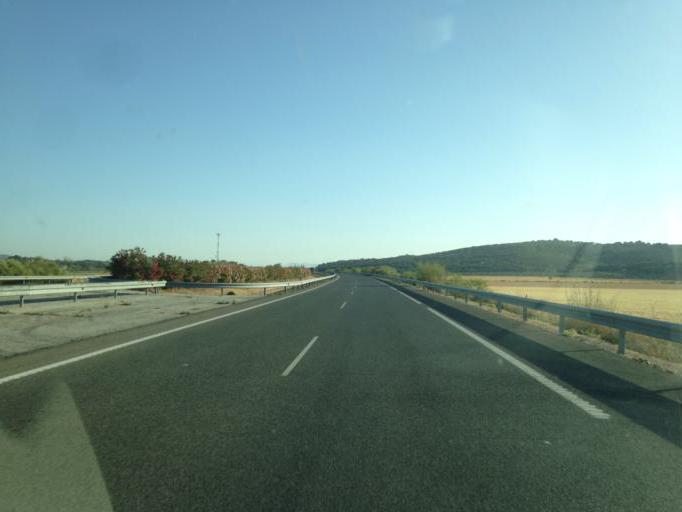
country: ES
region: Andalusia
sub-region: Provincia de Malaga
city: Villanueva del Trabuco
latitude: 37.0818
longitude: -4.3172
